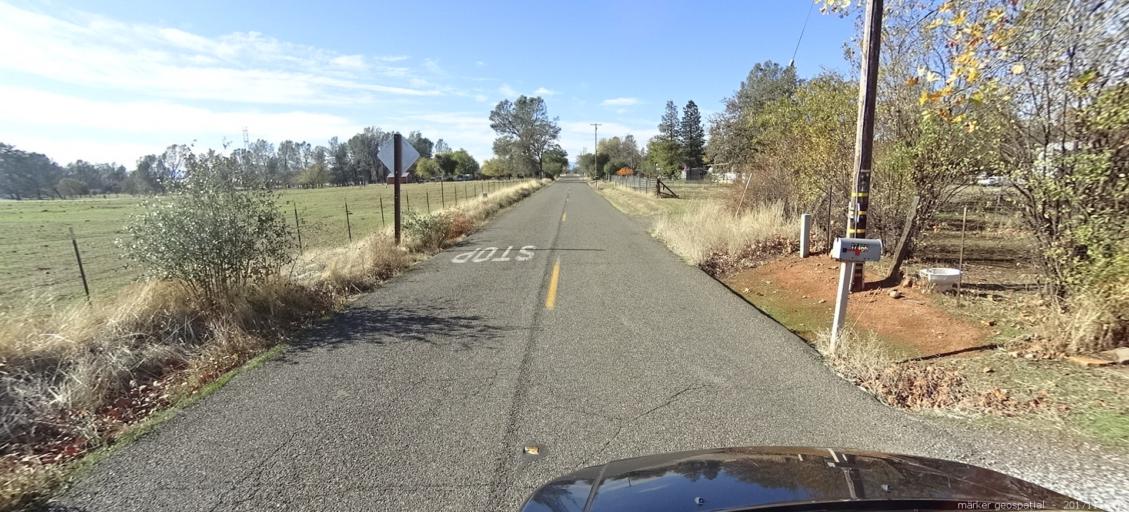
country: US
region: California
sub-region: Shasta County
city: Anderson
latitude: 40.4394
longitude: -122.4091
